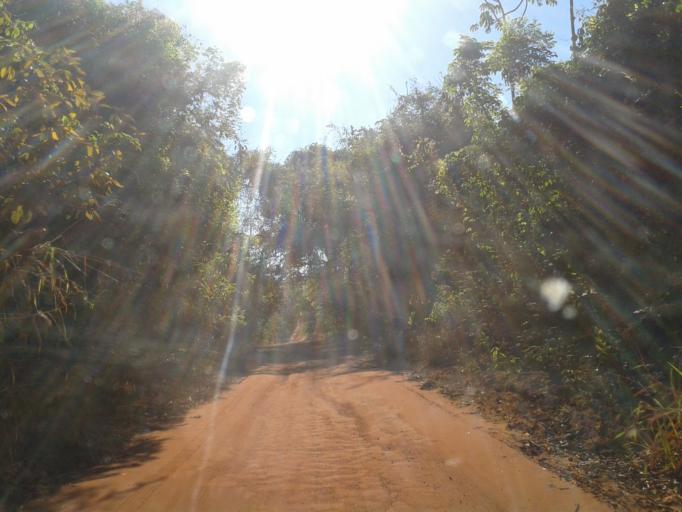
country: BR
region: Minas Gerais
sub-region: Ituiutaba
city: Ituiutaba
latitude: -19.0652
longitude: -49.3452
